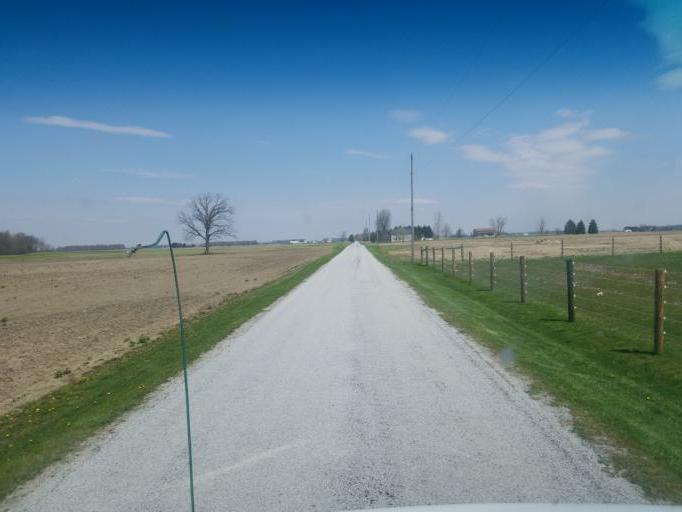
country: US
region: Ohio
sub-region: Hardin County
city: Kenton
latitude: 40.6899
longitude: -83.5474
